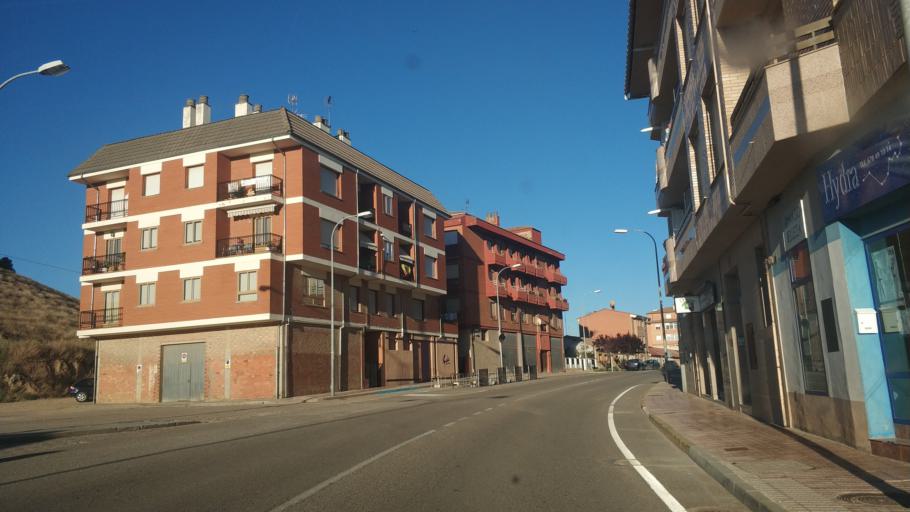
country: ES
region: Castille and Leon
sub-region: Provincia de Soria
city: San Esteban de Gormaz
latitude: 41.5727
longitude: -3.2003
